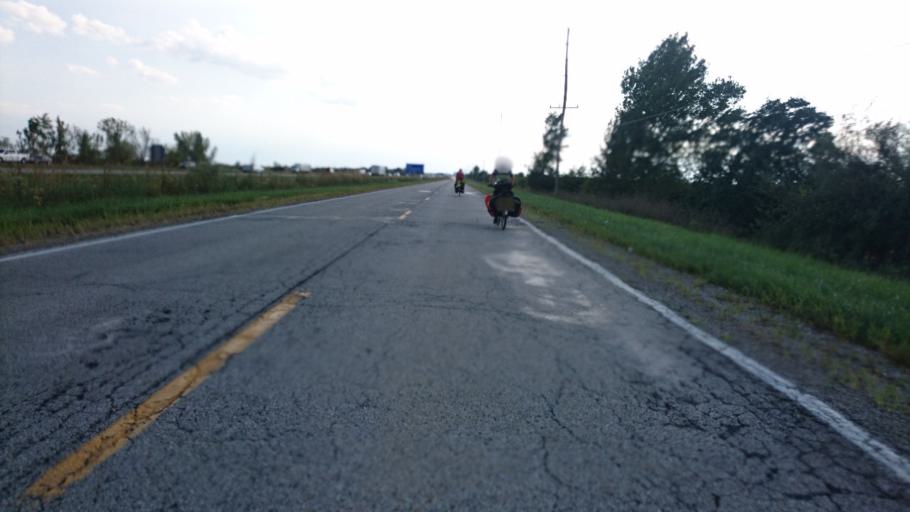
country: US
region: Illinois
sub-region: Logan County
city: Atlanta
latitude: 40.2905
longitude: -89.1974
